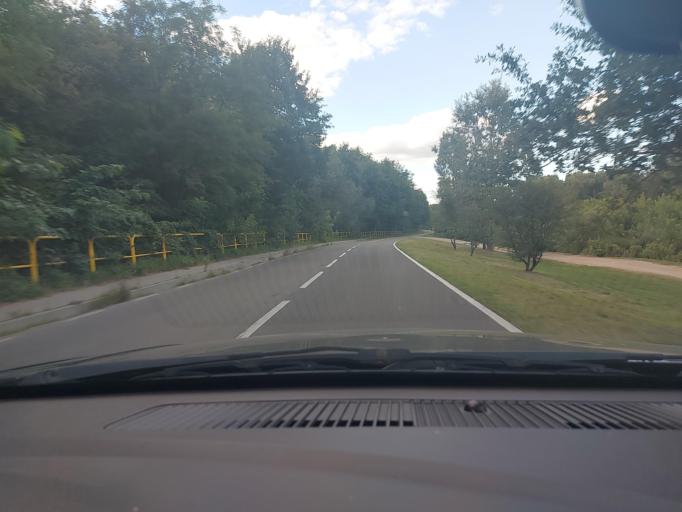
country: PL
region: Masovian Voivodeship
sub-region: Powiat nowodworski
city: Pomiechowek
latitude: 52.4811
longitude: 20.7210
